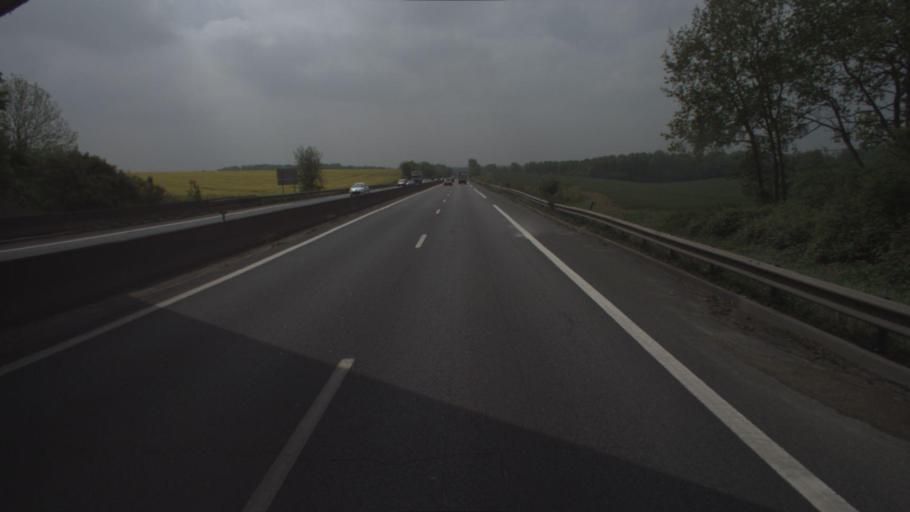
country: FR
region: Ile-de-France
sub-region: Departement de Seine-et-Marne
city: Longperrier
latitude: 49.0211
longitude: 2.6636
